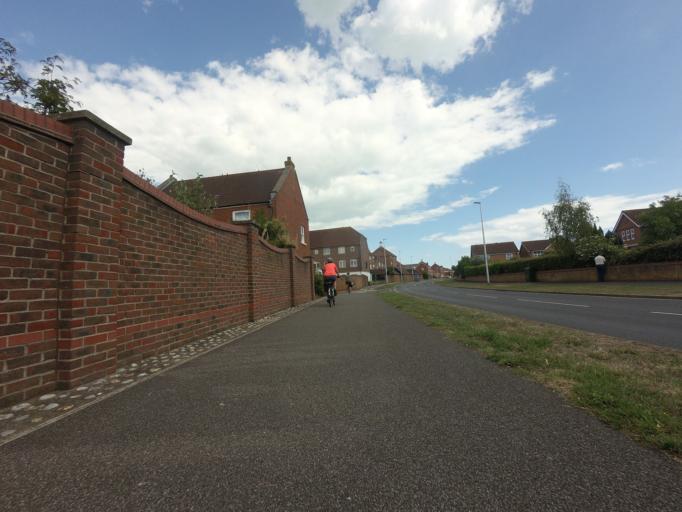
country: GB
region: England
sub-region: East Sussex
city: Pevensey
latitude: 50.7900
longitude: 0.3219
